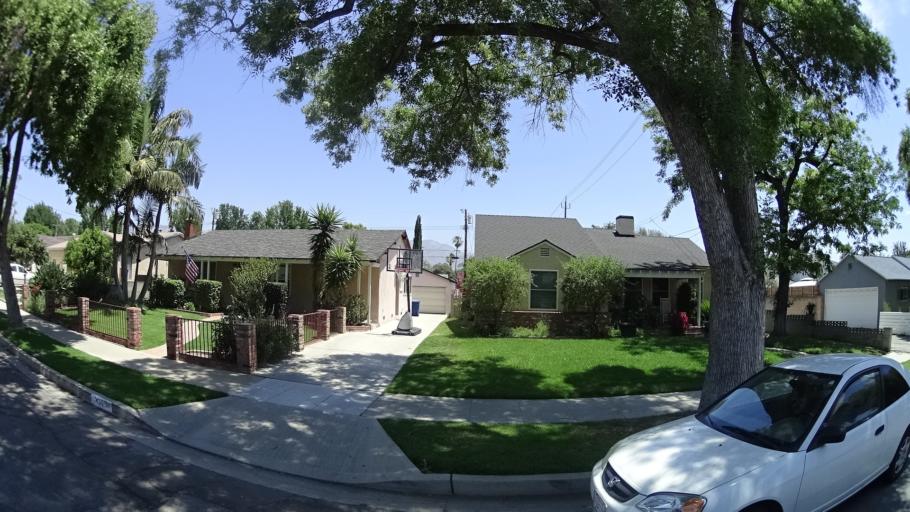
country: US
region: California
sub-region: Los Angeles County
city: Burbank
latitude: 34.1794
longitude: -118.3263
